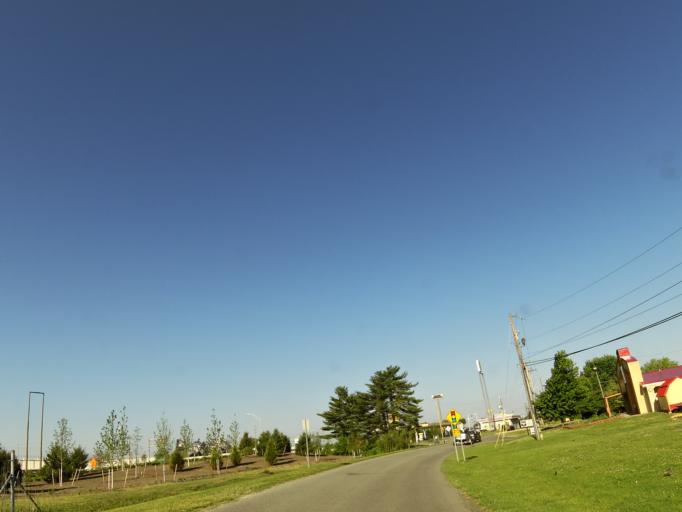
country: US
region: Indiana
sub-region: Jackson County
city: Seymour
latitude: 38.9590
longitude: -85.8467
